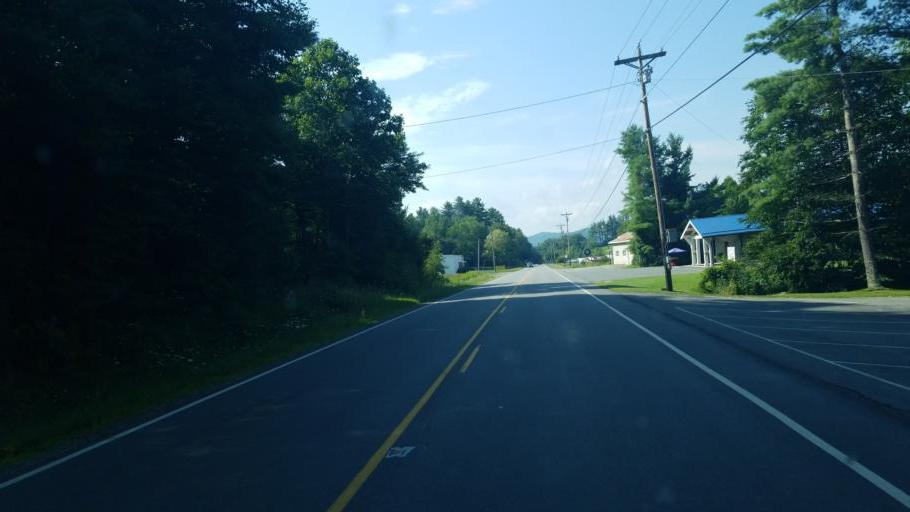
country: US
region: North Carolina
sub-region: Avery County
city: Newland
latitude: 36.0503
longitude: -81.9148
